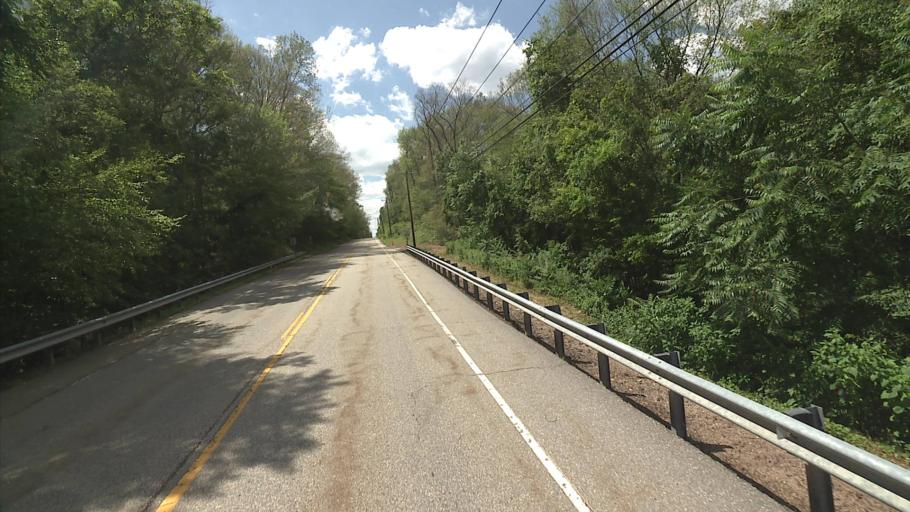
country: US
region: Connecticut
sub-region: Middlesex County
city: Higganum
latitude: 41.5212
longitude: -72.5095
